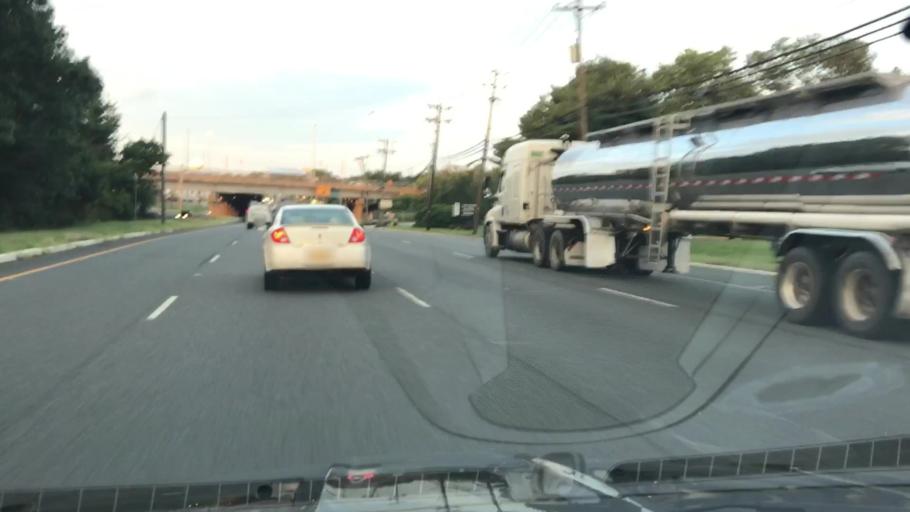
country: US
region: New Jersey
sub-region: Camden County
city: Pennsauken
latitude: 39.9745
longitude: -75.0331
